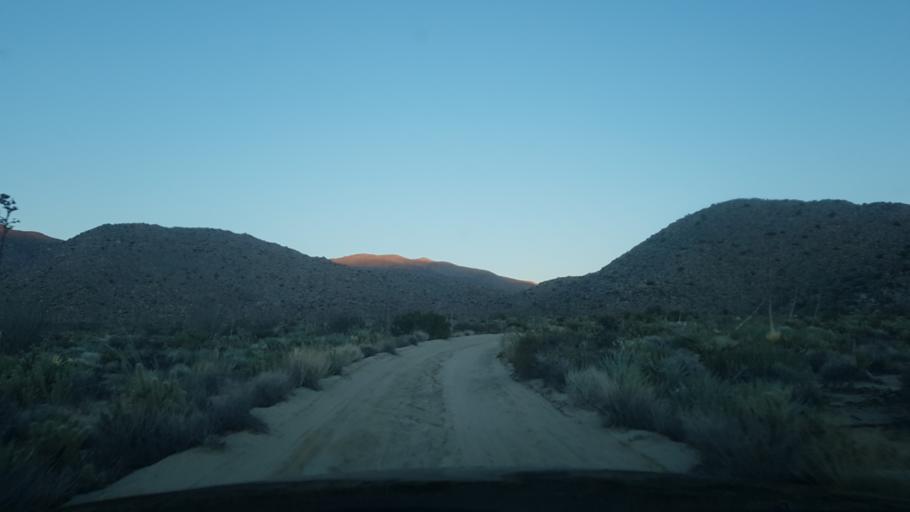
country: US
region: California
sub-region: San Diego County
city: Borrego Springs
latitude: 33.0178
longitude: -116.3691
